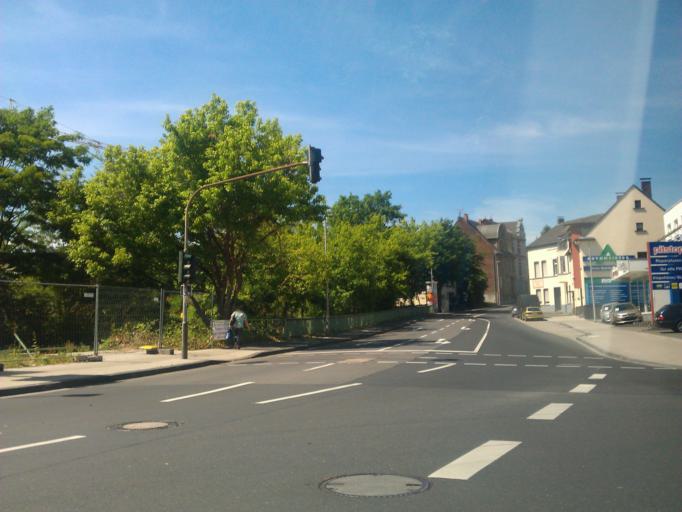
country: DE
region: North Rhine-Westphalia
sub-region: Regierungsbezirk Koln
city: Siegburg
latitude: 50.8011
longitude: 7.2024
